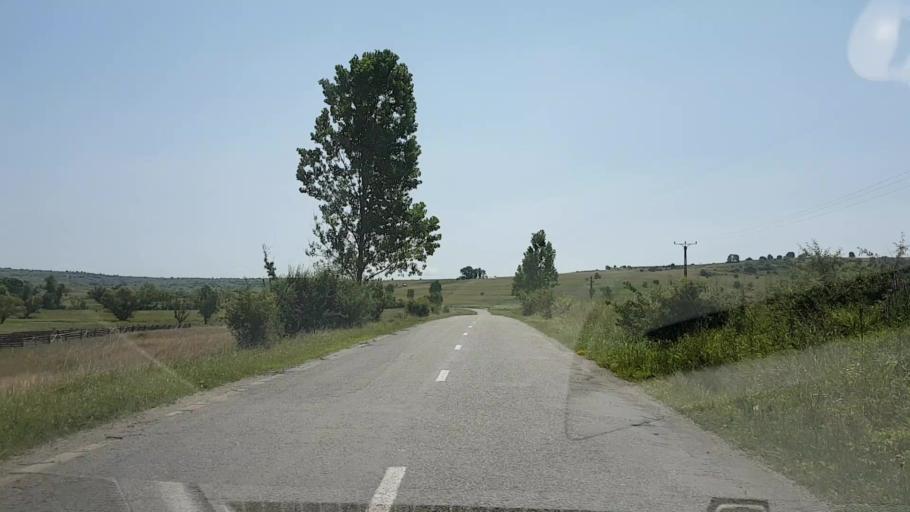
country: RO
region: Sibiu
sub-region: Comuna Merghindeal
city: Merghindeal
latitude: 45.9595
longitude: 24.7576
